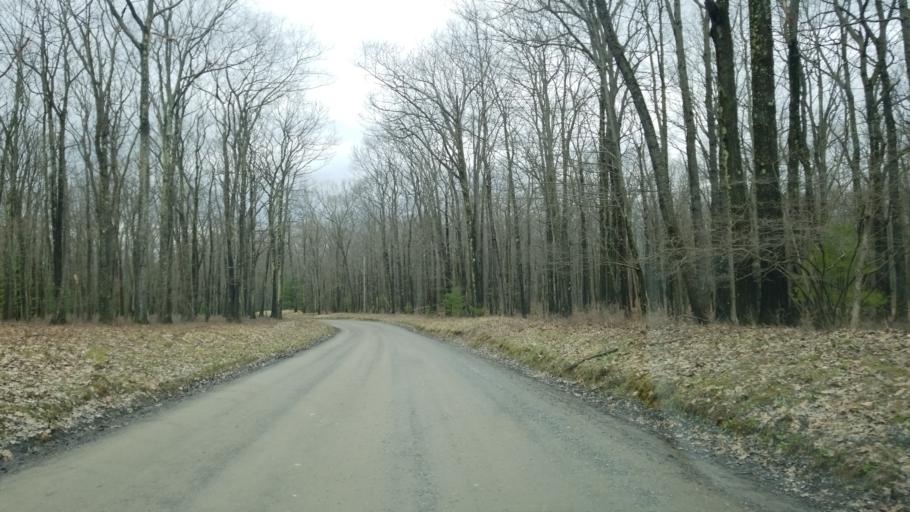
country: US
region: Pennsylvania
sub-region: Clearfield County
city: Shiloh
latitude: 41.1626
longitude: -78.3344
